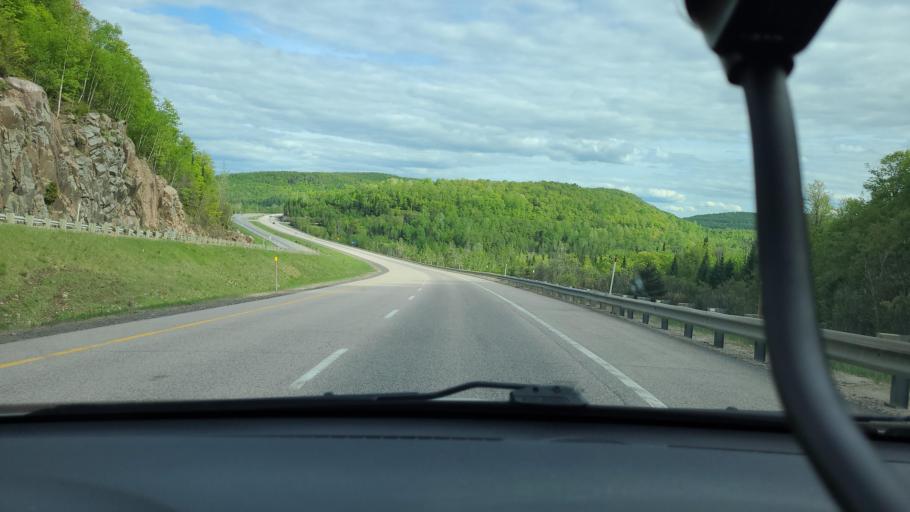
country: CA
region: Quebec
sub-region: Laurentides
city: Mont-Tremblant
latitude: 46.1481
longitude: -74.6610
